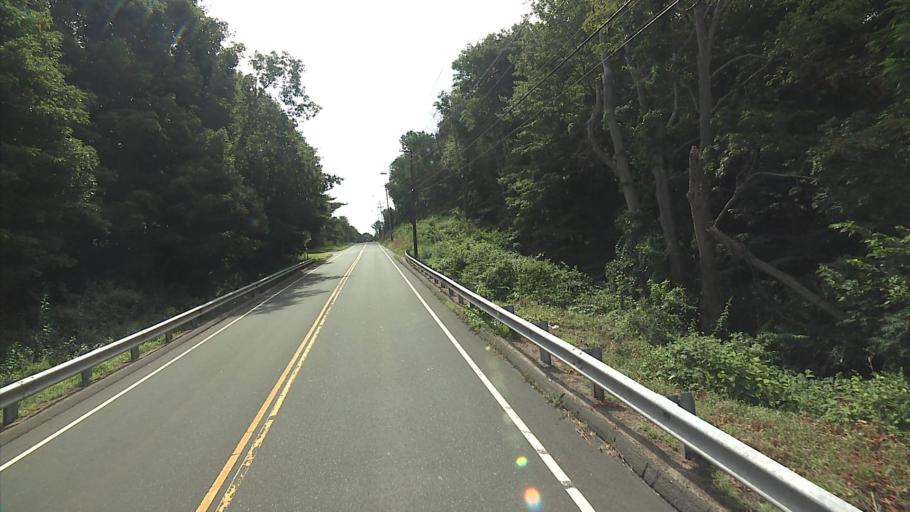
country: US
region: Connecticut
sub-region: New Haven County
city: Ansonia
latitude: 41.3298
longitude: -73.0640
